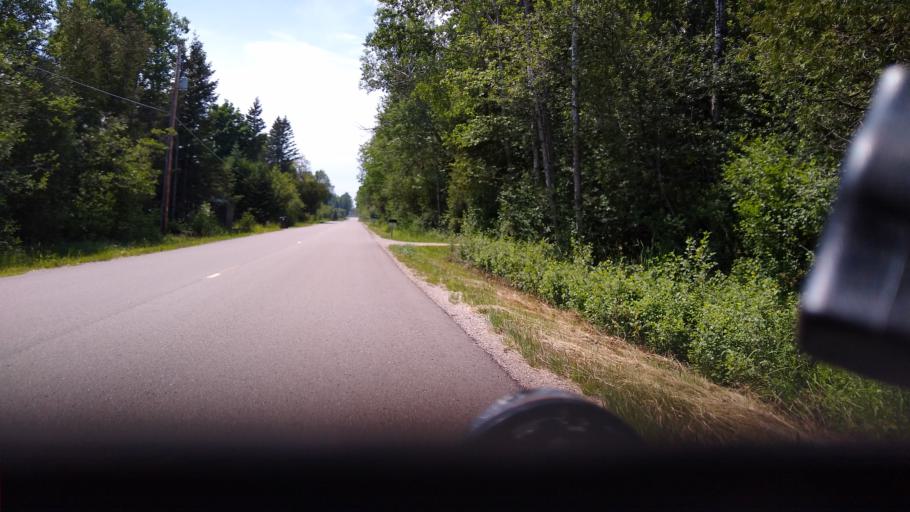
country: US
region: Michigan
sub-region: Delta County
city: Escanaba
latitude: 45.7100
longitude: -87.1131
